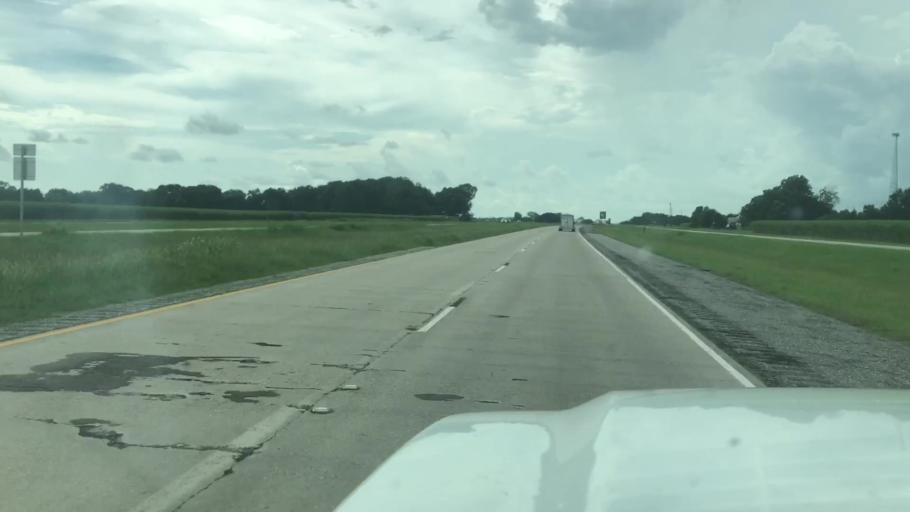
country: US
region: Louisiana
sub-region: Iberia Parish
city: Jeanerette
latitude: 29.8614
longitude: -91.6226
